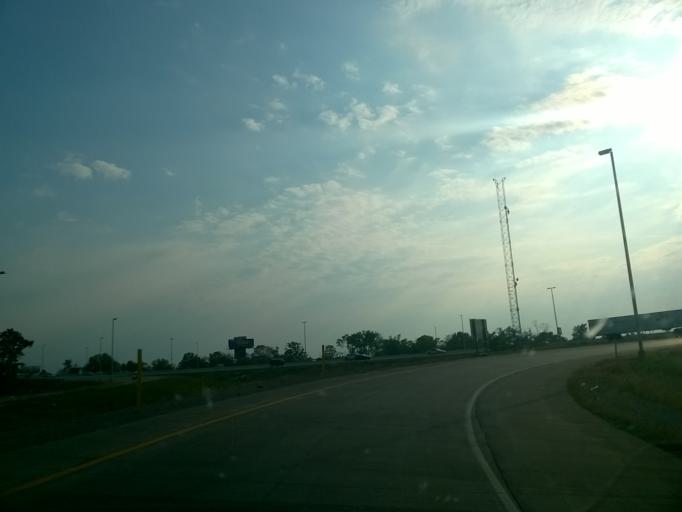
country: US
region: Indiana
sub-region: Marion County
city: Speedway
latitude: 39.7520
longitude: -86.2643
